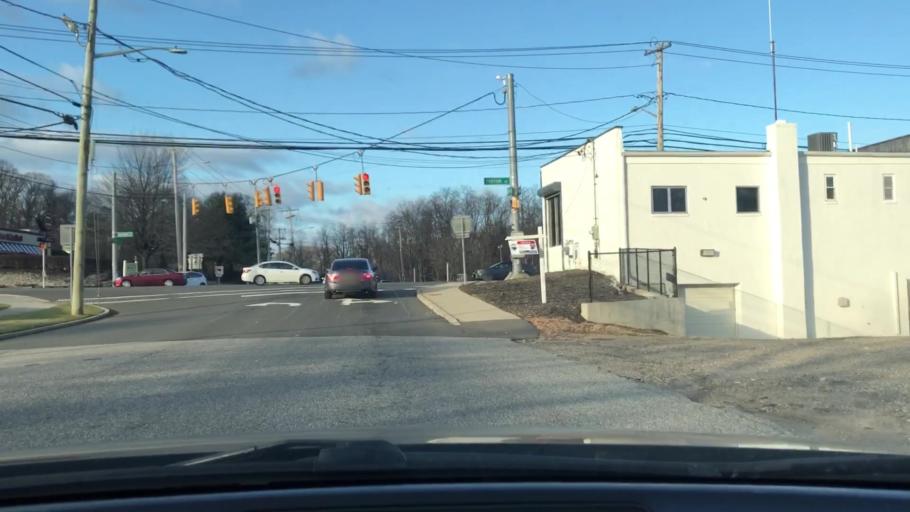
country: US
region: New York
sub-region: Suffolk County
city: Holbrook
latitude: 40.8311
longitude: -73.0864
